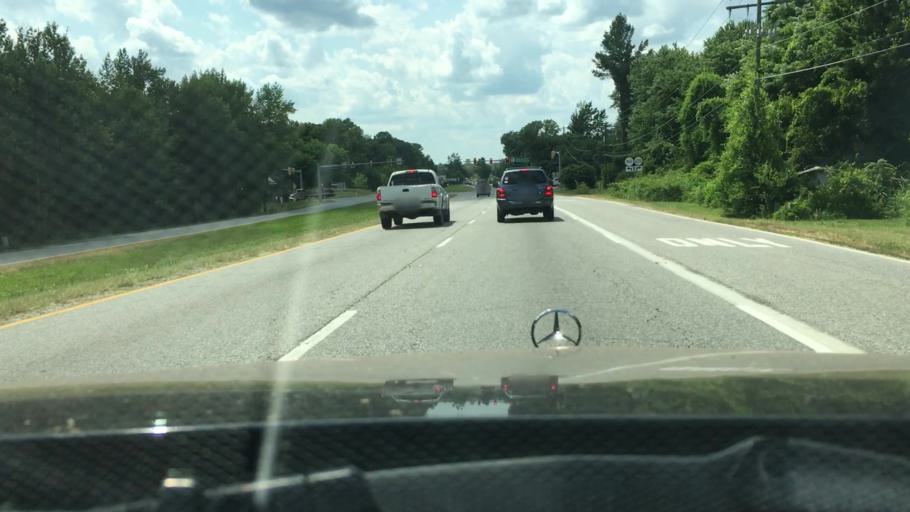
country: US
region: Virginia
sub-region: Spotsylvania County
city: Spotsylvania
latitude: 38.2923
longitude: -77.5746
